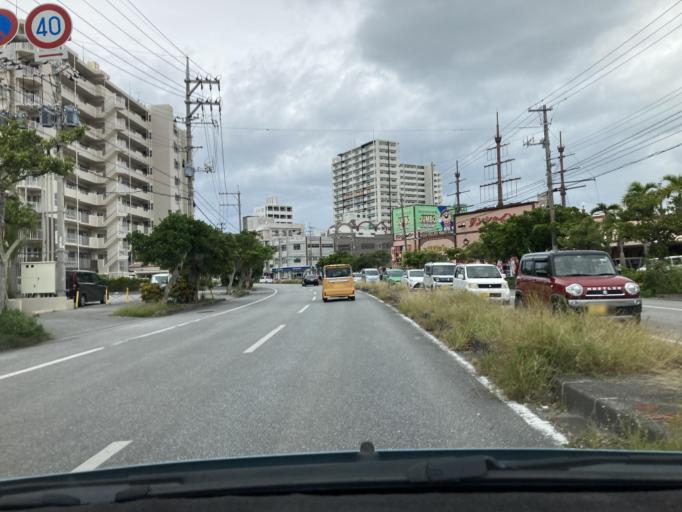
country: JP
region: Okinawa
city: Itoman
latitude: 26.1413
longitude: 127.6715
